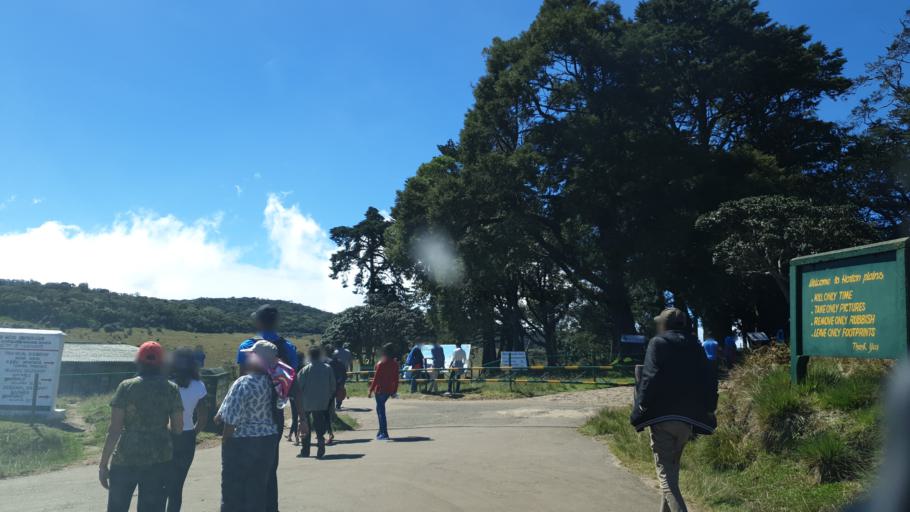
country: LK
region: Uva
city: Haputale
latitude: 6.8021
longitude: 80.8074
